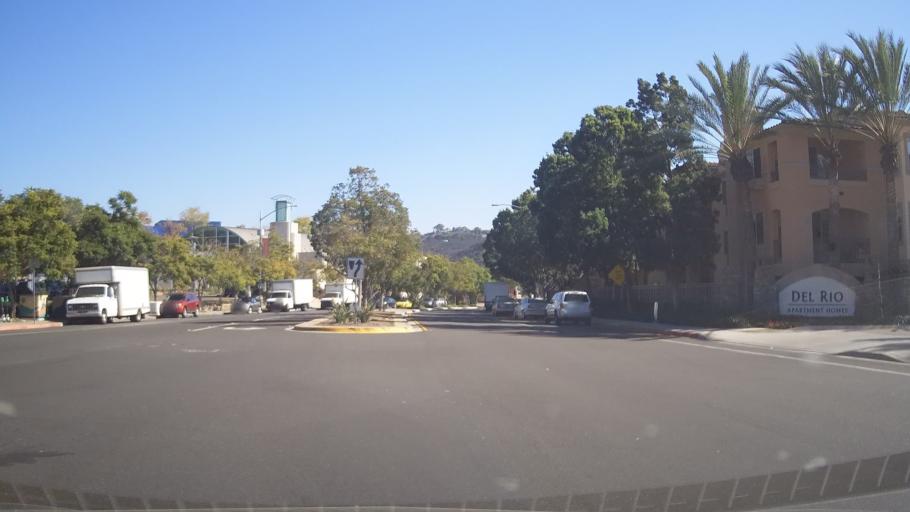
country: US
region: California
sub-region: San Diego County
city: San Diego
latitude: 32.7797
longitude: -117.1284
